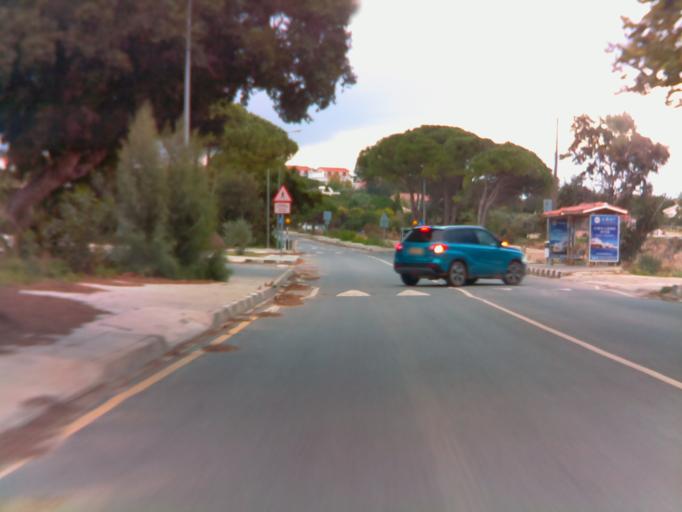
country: CY
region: Pafos
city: Pegeia
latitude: 34.8553
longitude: 32.3695
